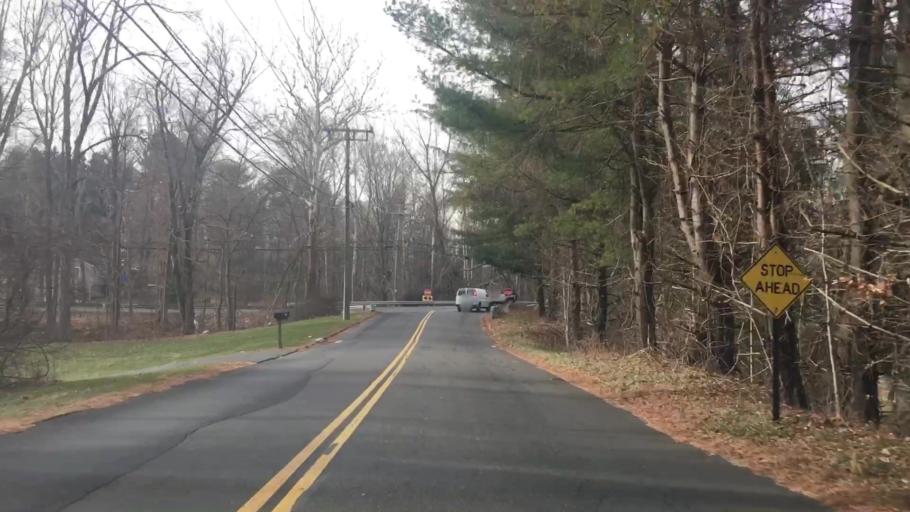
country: US
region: Connecticut
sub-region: Fairfield County
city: Bethel
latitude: 41.4392
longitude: -73.3906
